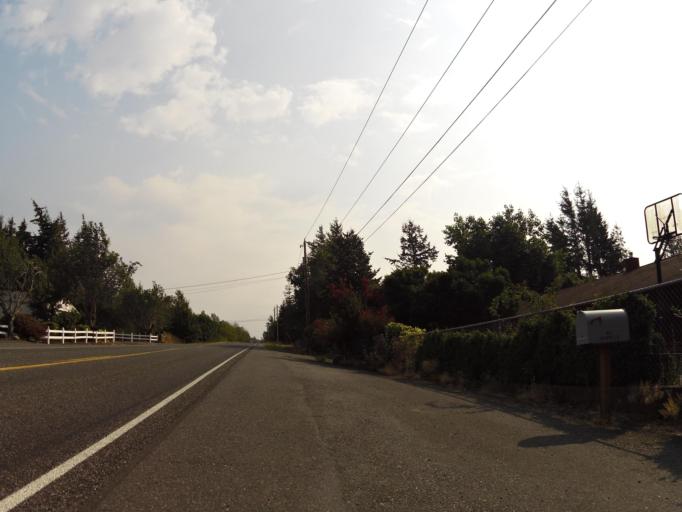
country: US
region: Washington
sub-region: Whatcom County
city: Marietta
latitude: 48.7897
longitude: -122.5689
